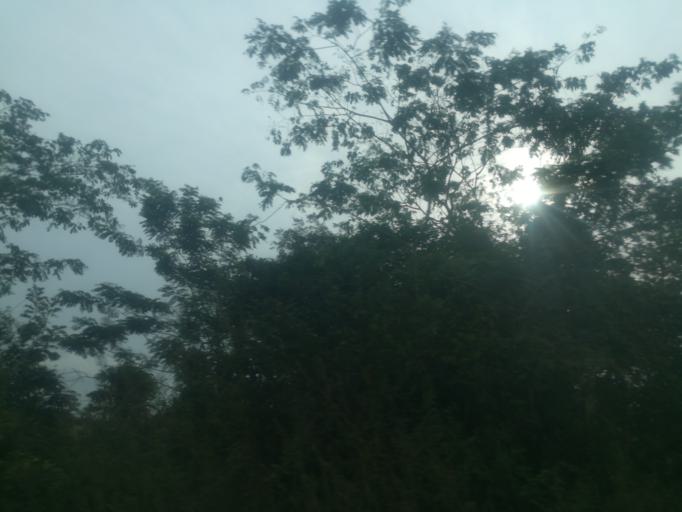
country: NG
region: Ogun
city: Ayetoro
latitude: 7.2659
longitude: 3.1082
